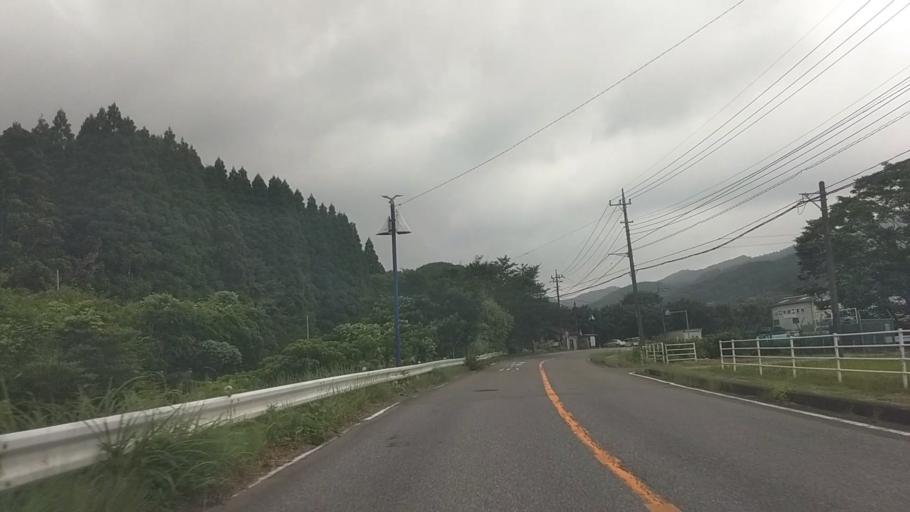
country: JP
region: Chiba
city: Kawaguchi
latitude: 35.1381
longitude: 139.9787
